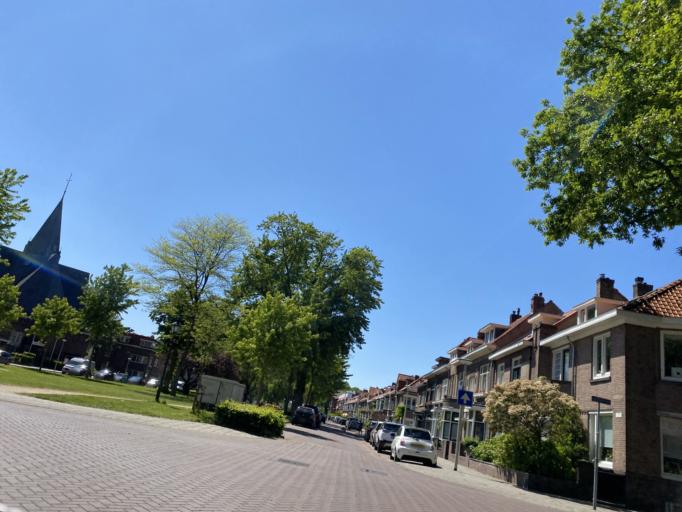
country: NL
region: North Brabant
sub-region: Gemeente Bergen op Zoom
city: Bergen op Zoom
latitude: 51.4995
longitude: 4.2871
